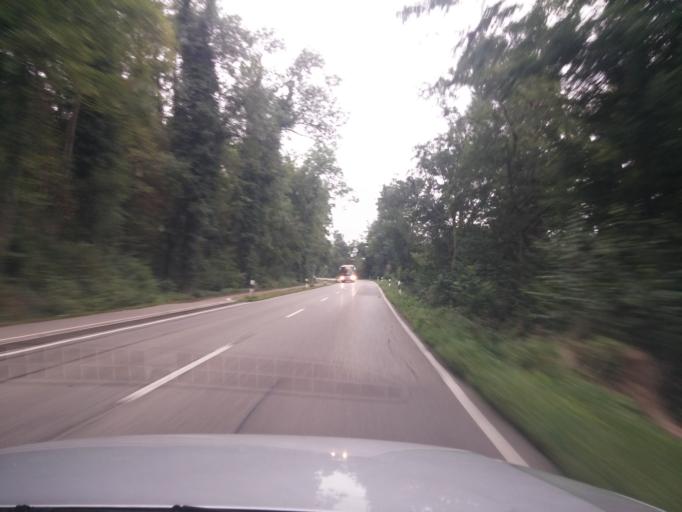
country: DE
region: Baden-Wuerttemberg
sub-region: Tuebingen Region
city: Aitrach
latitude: 47.9474
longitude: 10.1106
